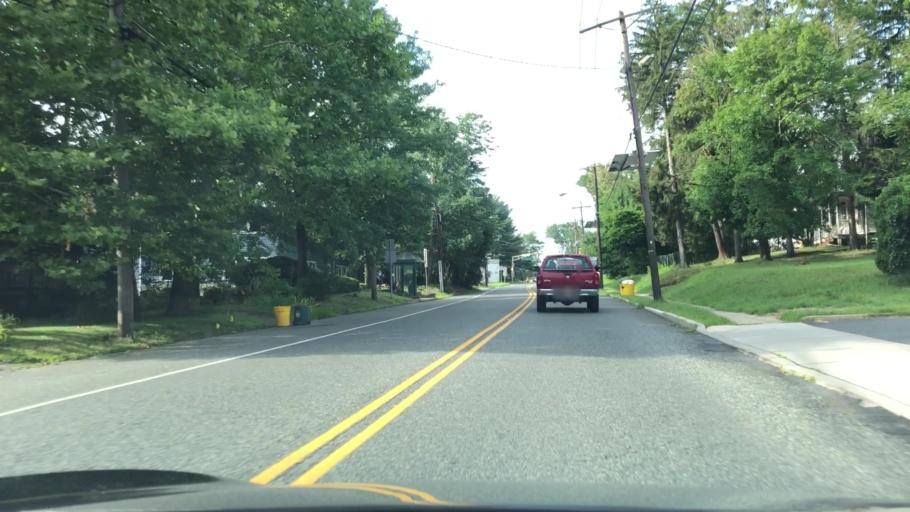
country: US
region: New Jersey
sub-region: Mercer County
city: Prospect Park
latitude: 40.2513
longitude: -74.7424
